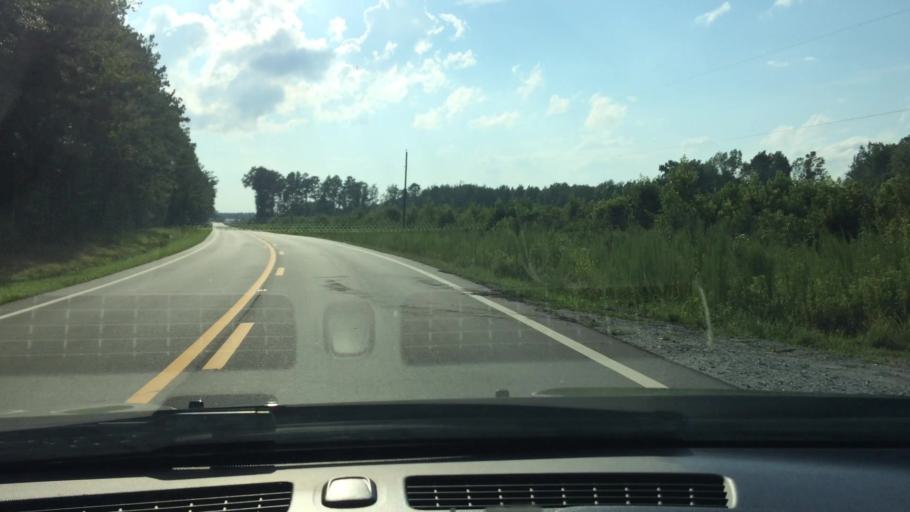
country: US
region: North Carolina
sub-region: Craven County
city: Vanceboro
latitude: 35.4379
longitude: -77.1438
